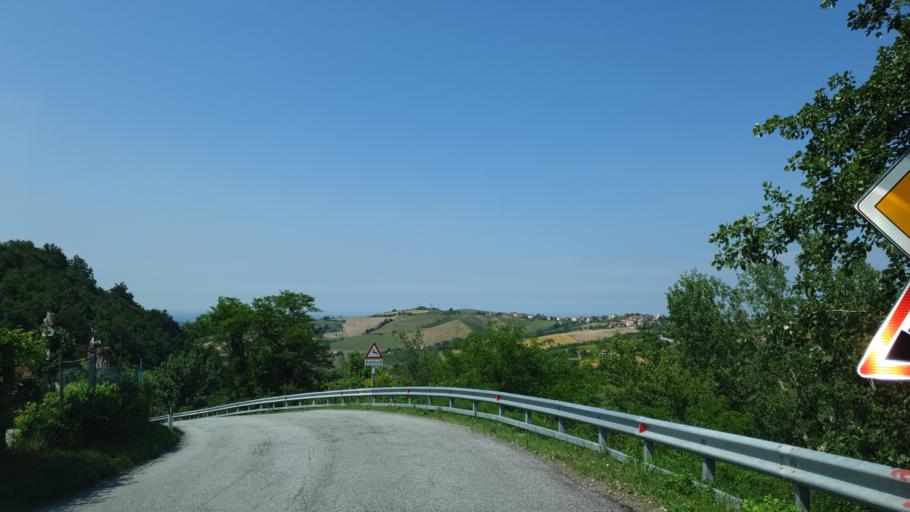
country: SM
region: San Marino
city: San Marino
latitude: 43.9376
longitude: 12.4335
